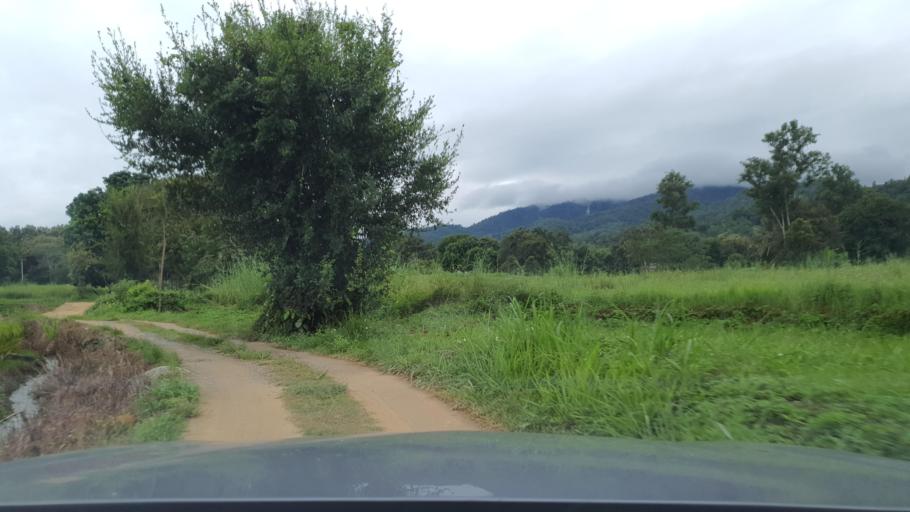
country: TH
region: Chiang Mai
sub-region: Amphoe Chiang Dao
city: Chiang Dao
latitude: 19.3326
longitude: 98.9347
